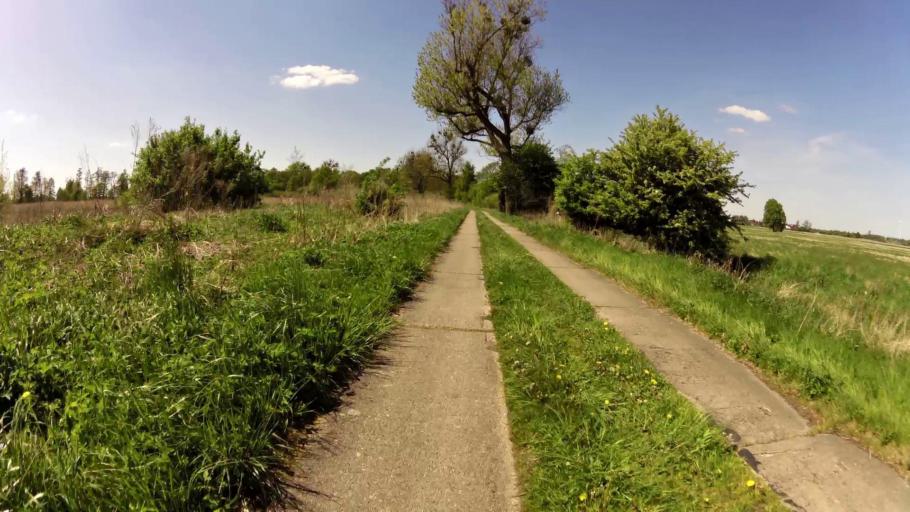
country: PL
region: West Pomeranian Voivodeship
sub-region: Powiat bialogardzki
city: Bialogard
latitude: 54.0024
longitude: 16.0184
